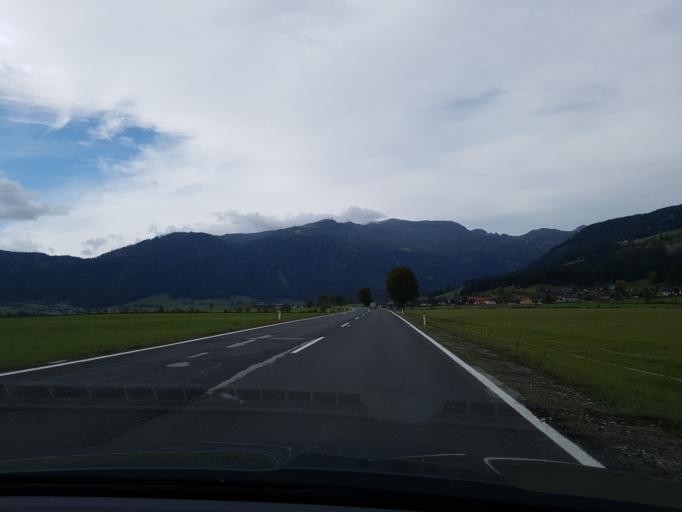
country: AT
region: Salzburg
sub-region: Politischer Bezirk Tamsweg
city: Mauterndorf
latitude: 47.1407
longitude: 13.7146
